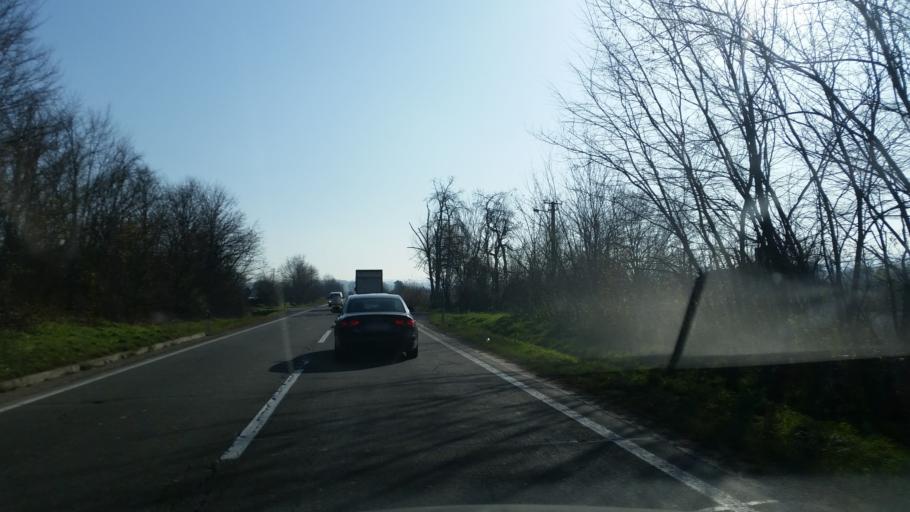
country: RS
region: Central Serbia
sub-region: Kolubarski Okrug
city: Ljig
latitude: 44.2878
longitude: 20.2701
